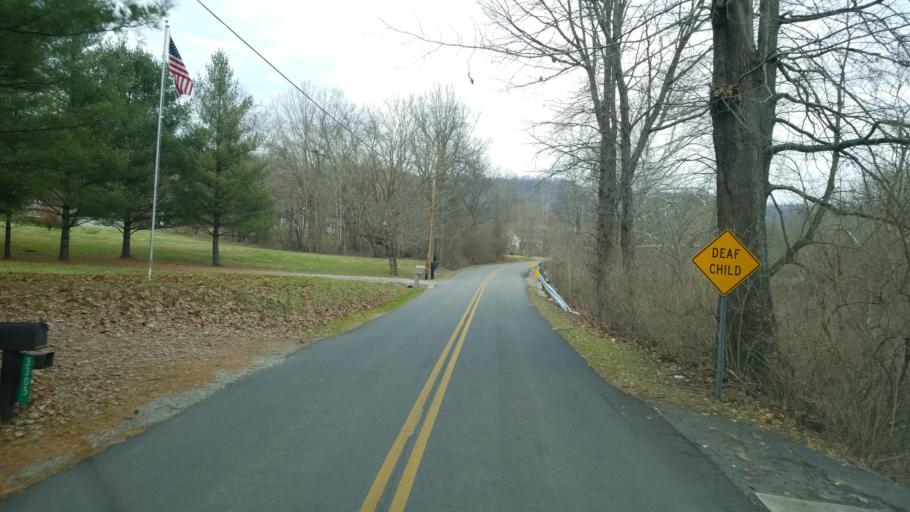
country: US
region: Ohio
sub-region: Highland County
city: Greenfield
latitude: 39.2354
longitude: -83.2881
